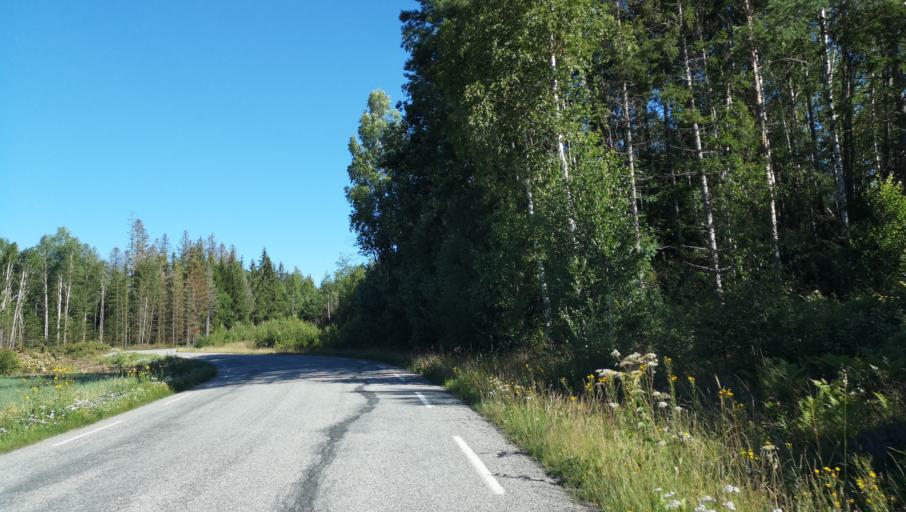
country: NO
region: Ostfold
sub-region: Hobol
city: Knappstad
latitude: 59.6416
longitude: 11.0163
